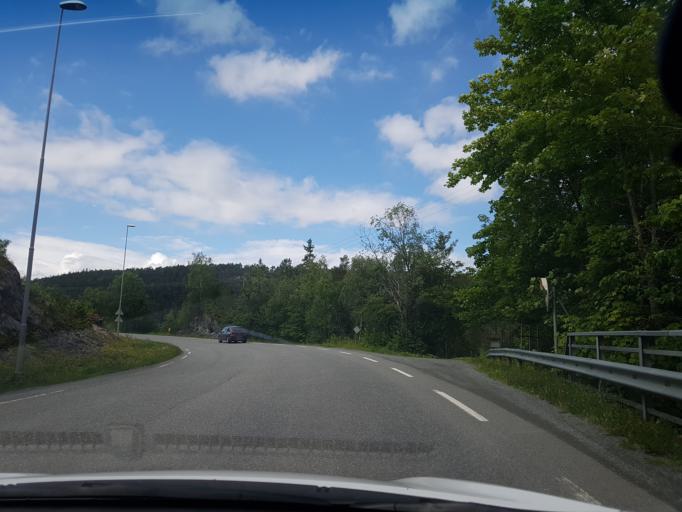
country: NO
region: Nord-Trondelag
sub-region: Stjordal
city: Stjordalshalsen
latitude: 63.6044
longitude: 10.9601
